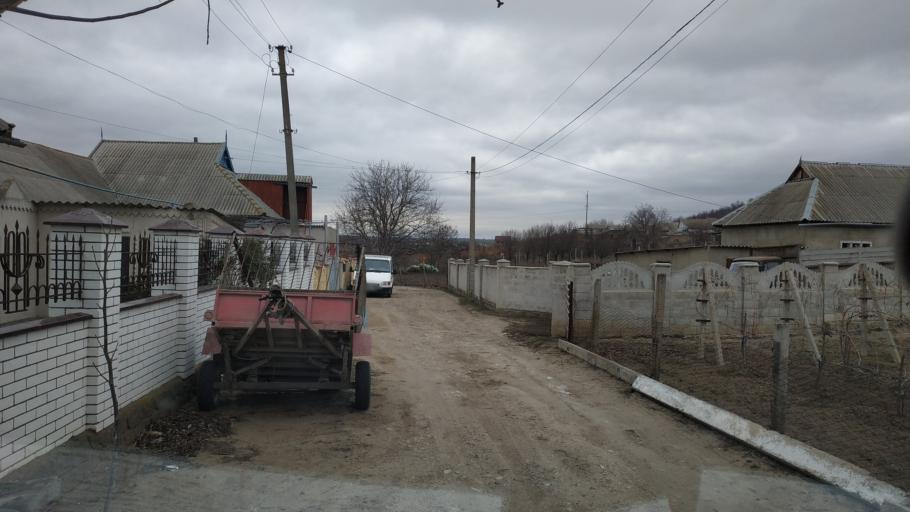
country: MD
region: Causeni
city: Causeni
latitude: 46.6562
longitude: 29.4431
